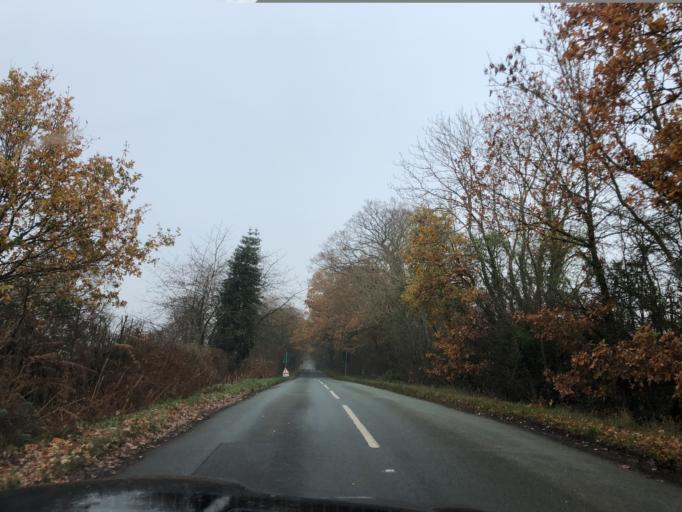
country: GB
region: England
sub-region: Solihull
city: Balsall Common
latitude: 52.3683
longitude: -1.6568
